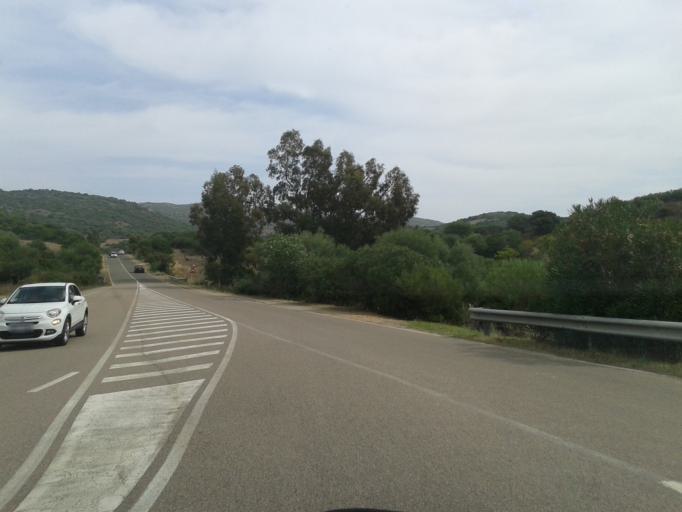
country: IT
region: Sardinia
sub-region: Provincia di Cagliari
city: Villasimius
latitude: 39.1368
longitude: 9.5366
